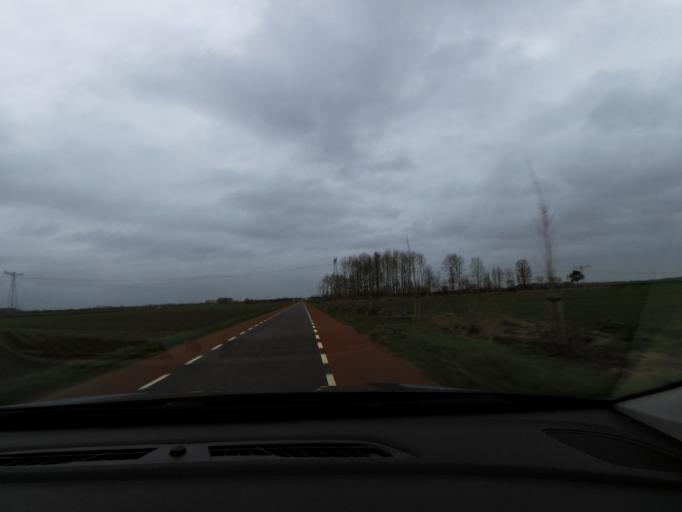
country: NL
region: North Brabant
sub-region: Gemeente Waalwijk
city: Waspik
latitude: 51.7087
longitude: 4.9841
